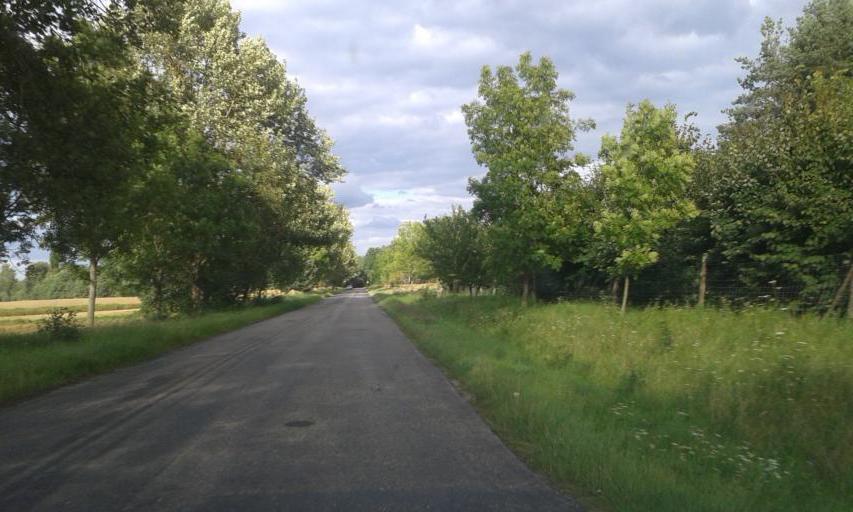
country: PL
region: West Pomeranian Voivodeship
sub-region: Powiat bialogardzki
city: Tychowo
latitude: 53.8992
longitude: 16.2133
